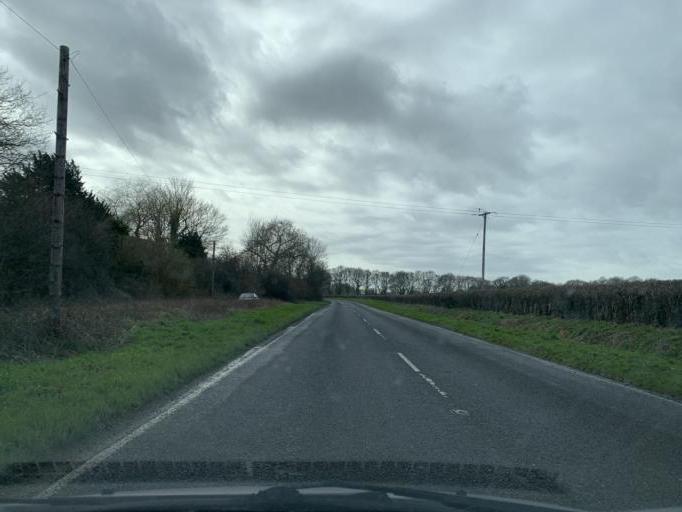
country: GB
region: England
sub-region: Wiltshire
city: Downton
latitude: 50.9691
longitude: -1.7680
